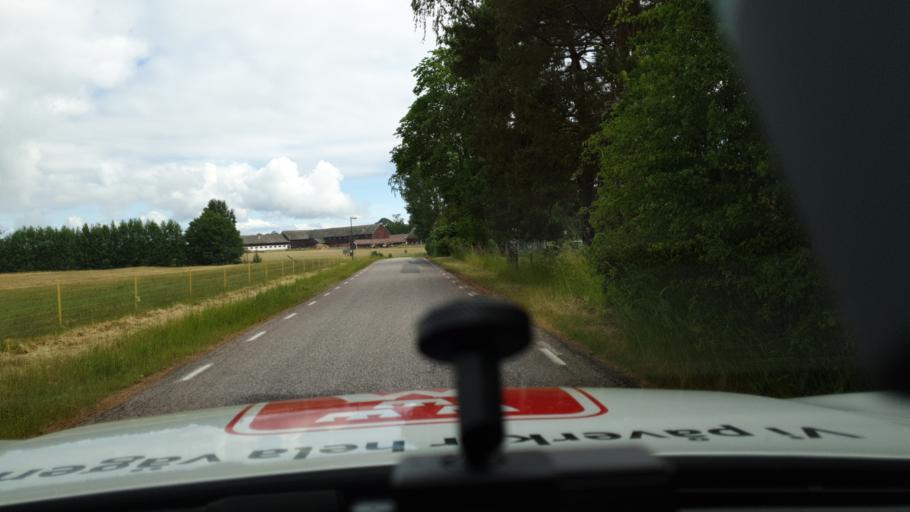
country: SE
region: Vaestra Goetaland
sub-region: Karlsborgs Kommun
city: Molltorp
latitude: 58.4359
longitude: 14.3979
